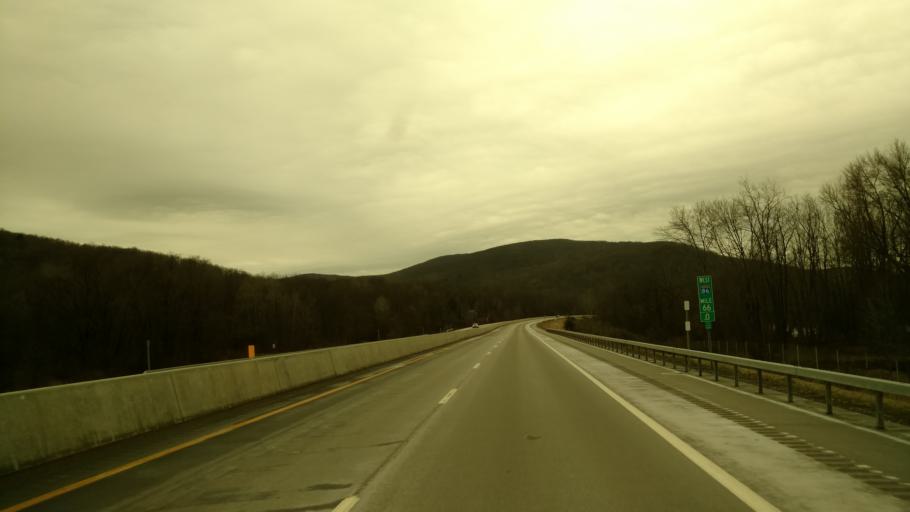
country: US
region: New York
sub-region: Cattaraugus County
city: Salamanca
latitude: 42.0975
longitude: -78.6571
